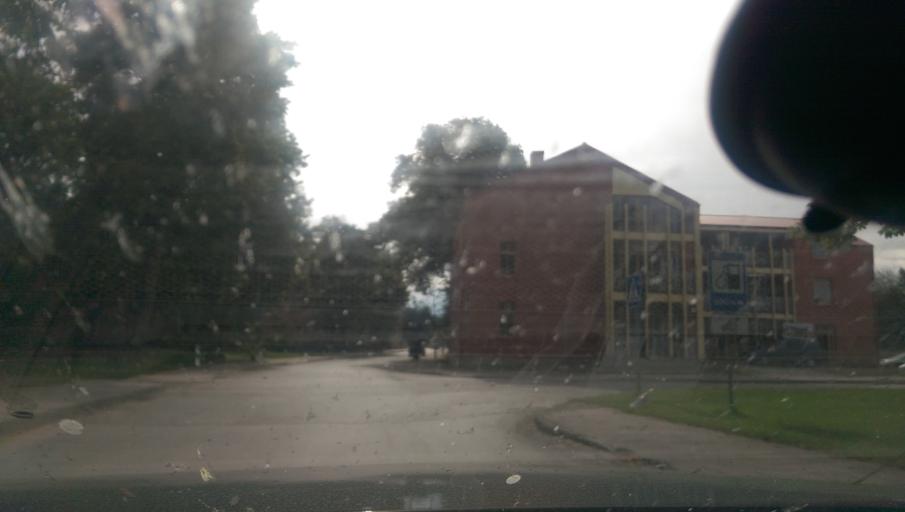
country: LT
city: Rusne
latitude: 55.2972
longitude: 21.3749
